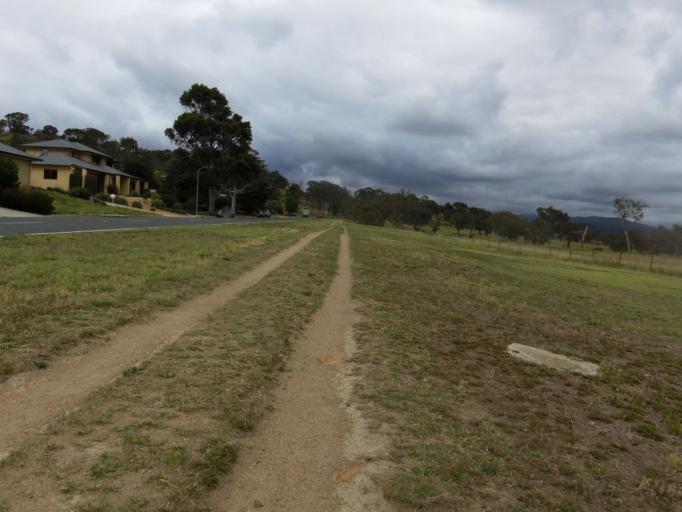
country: AU
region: Australian Capital Territory
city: Macquarie
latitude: -35.3484
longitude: 149.0258
